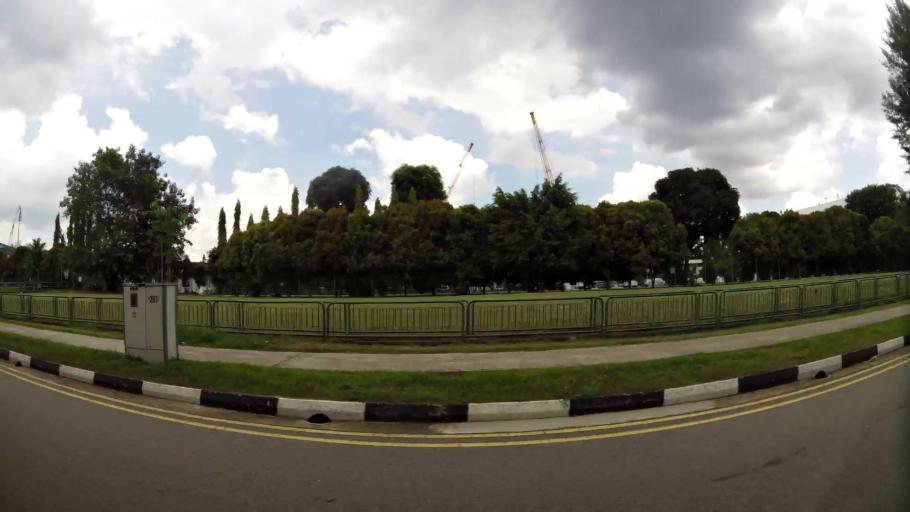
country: MY
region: Johor
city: Kampung Pasir Gudang Baru
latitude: 1.4599
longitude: 103.8213
